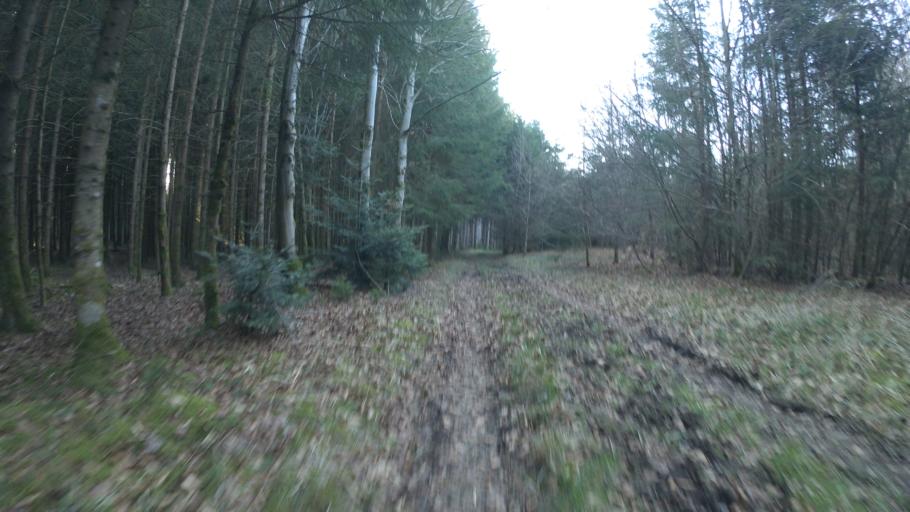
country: DE
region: Bavaria
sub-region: Upper Bavaria
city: Traunreut
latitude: 47.9361
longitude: 12.5716
